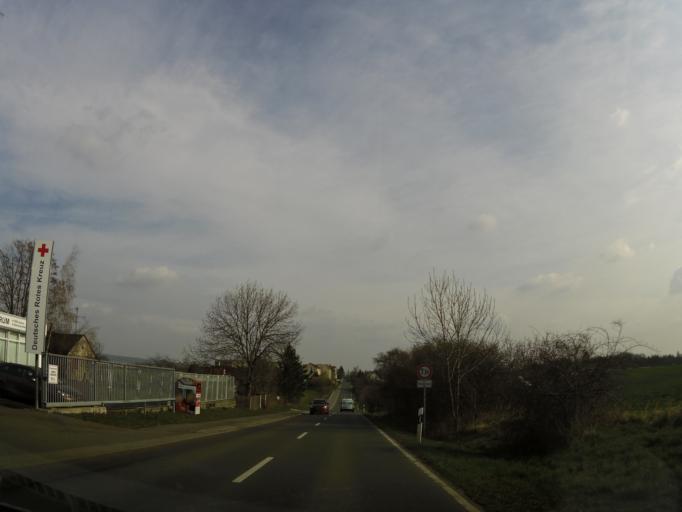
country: DE
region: Thuringia
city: Weimar
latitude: 50.9645
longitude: 11.3124
